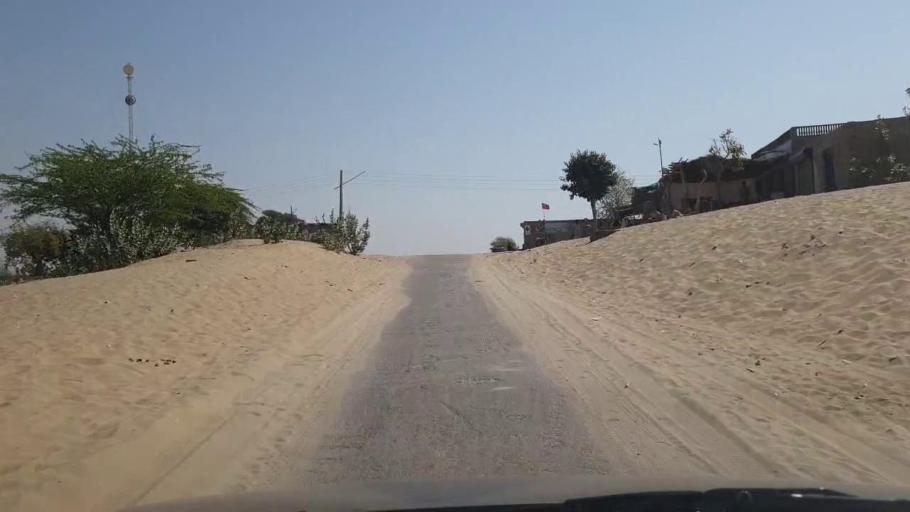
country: PK
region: Sindh
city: Chor
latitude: 25.6007
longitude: 69.9987
